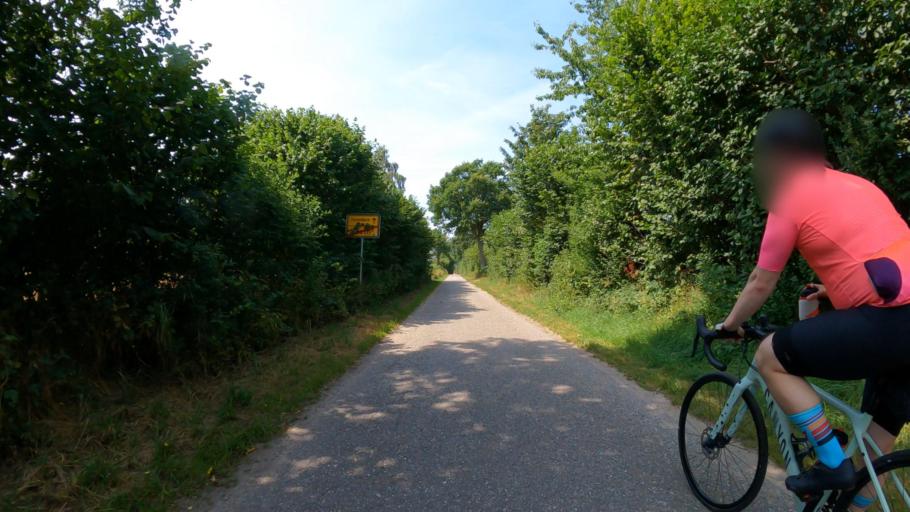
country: DE
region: Schleswig-Holstein
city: Seth
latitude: 53.8471
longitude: 10.1685
